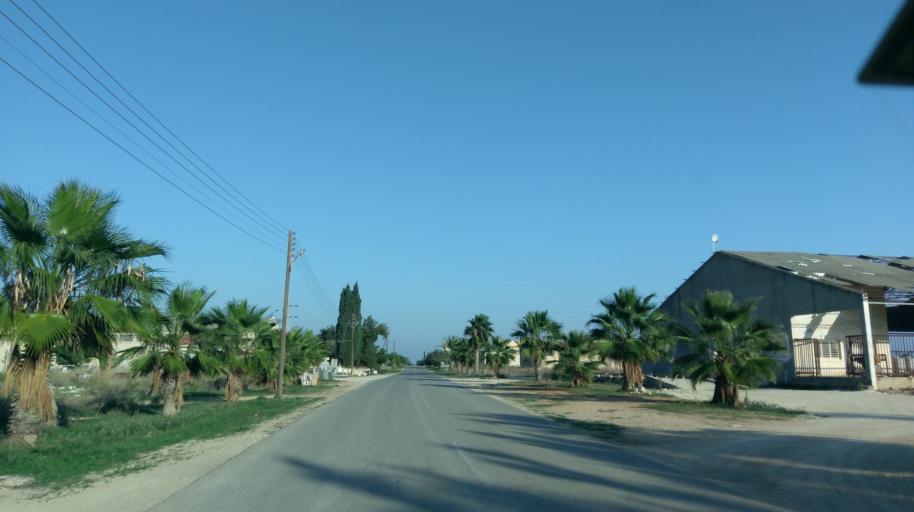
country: CY
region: Ammochostos
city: Leonarisso
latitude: 35.4240
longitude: 34.0873
